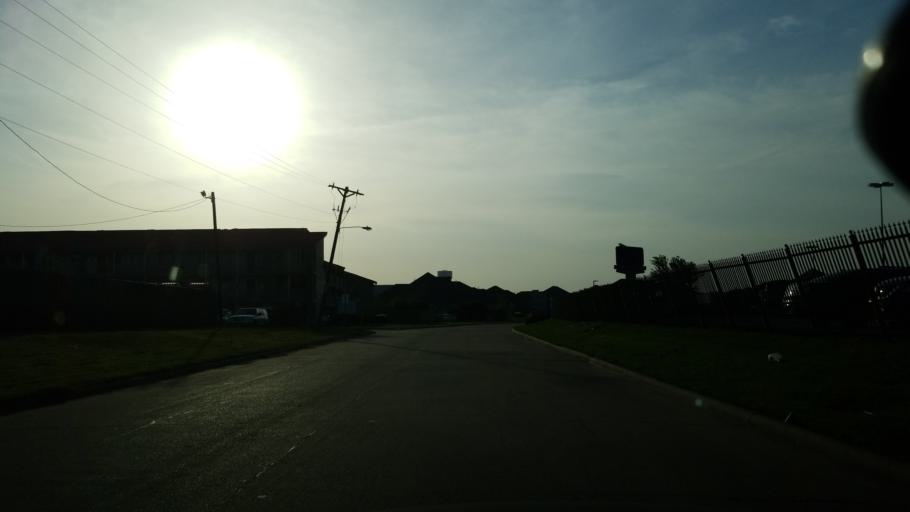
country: US
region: Texas
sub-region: Dallas County
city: Coppell
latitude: 32.9120
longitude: -97.0060
